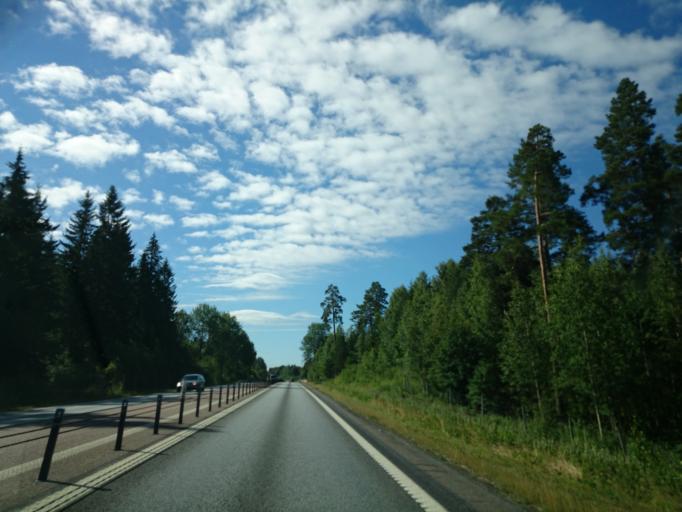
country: SE
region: Gaevleborg
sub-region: Soderhamns Kommun
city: Soderhamn
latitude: 61.2540
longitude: 17.0345
